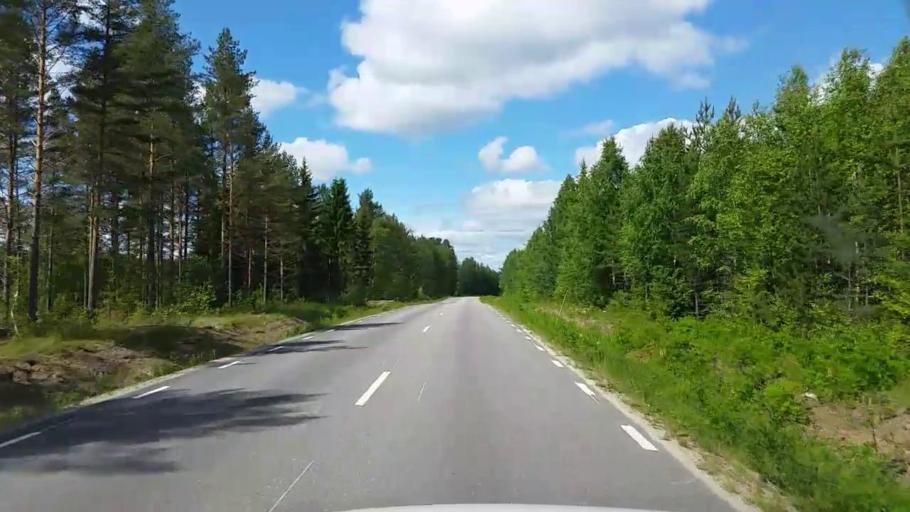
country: SE
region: Gaevleborg
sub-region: Ovanakers Kommun
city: Alfta
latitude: 61.2657
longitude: 16.1208
